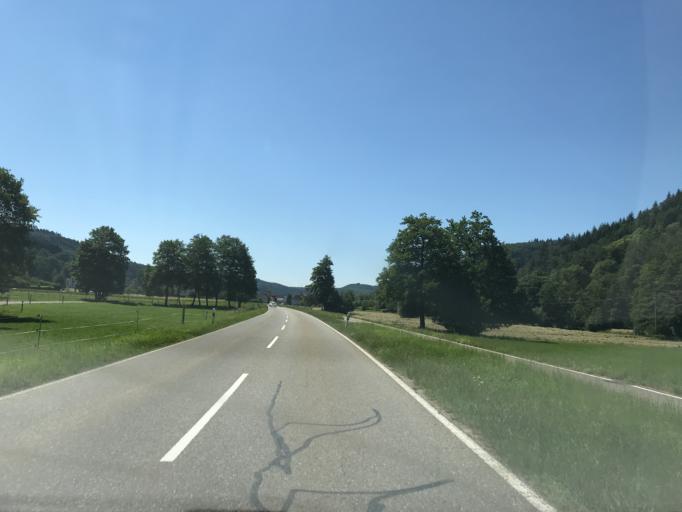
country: DE
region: Baden-Wuerttemberg
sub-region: Freiburg Region
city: Schopfheim
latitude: 47.6692
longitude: 7.8020
